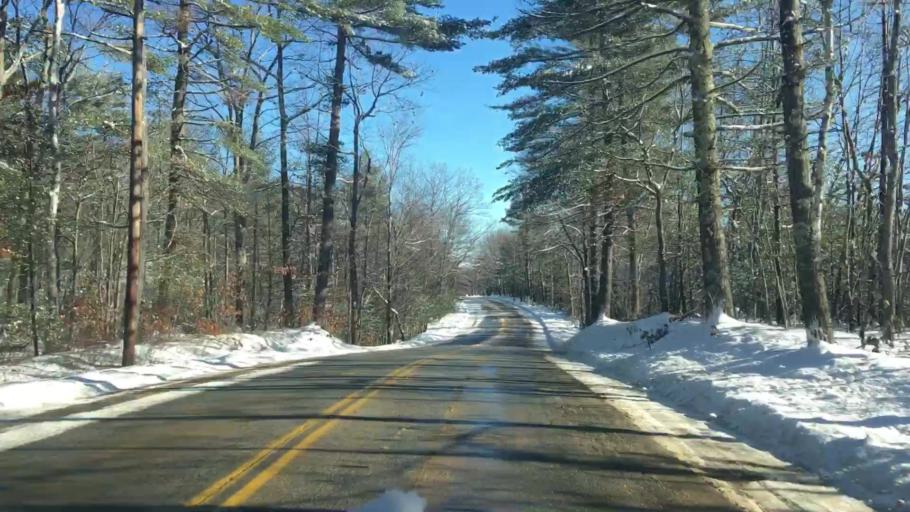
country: US
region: Maine
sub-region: Cumberland County
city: New Gloucester
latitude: 43.9629
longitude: -70.3422
